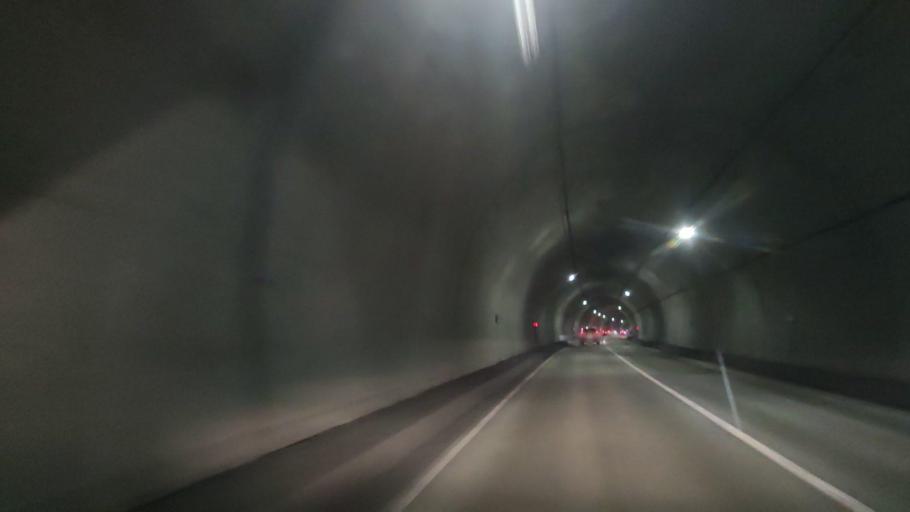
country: JP
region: Hokkaido
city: Ishikari
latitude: 43.5209
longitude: 141.3920
